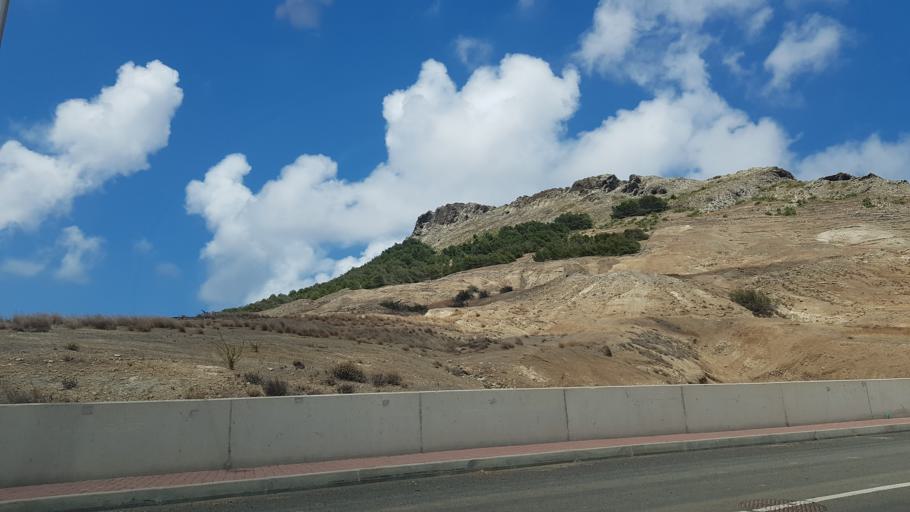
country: PT
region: Madeira
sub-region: Porto Santo
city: Vila de Porto Santo
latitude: 33.0461
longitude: -16.3639
